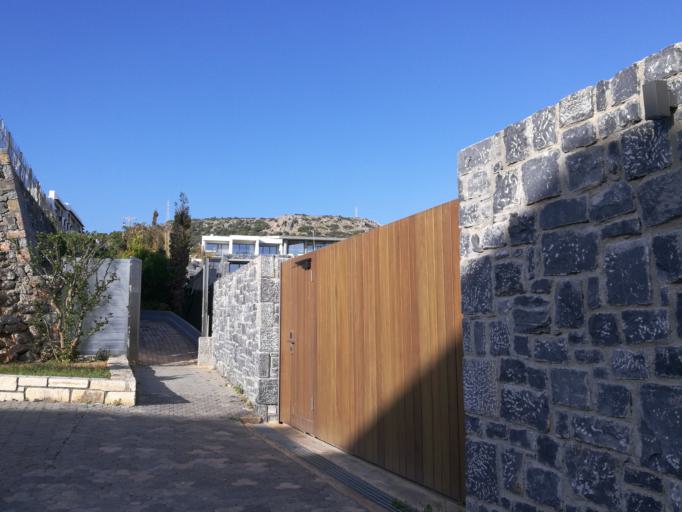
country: GR
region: Crete
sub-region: Nomos Irakleiou
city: Stalis
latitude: 35.3046
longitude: 25.4200
